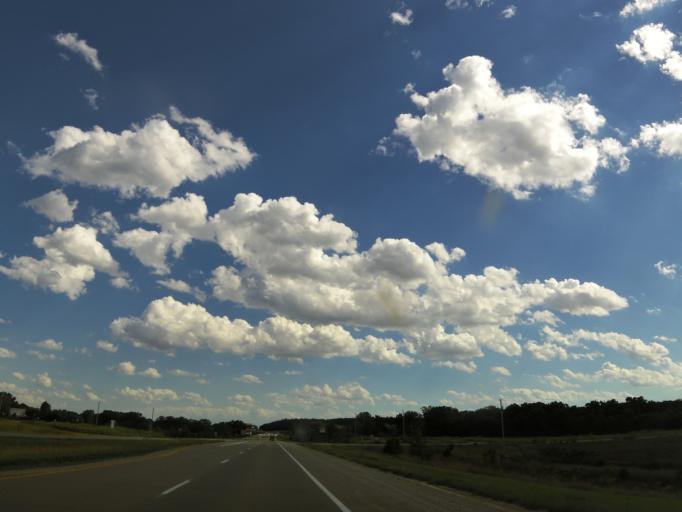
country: US
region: Missouri
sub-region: Clark County
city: Kahoka
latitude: 40.4683
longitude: -91.5683
